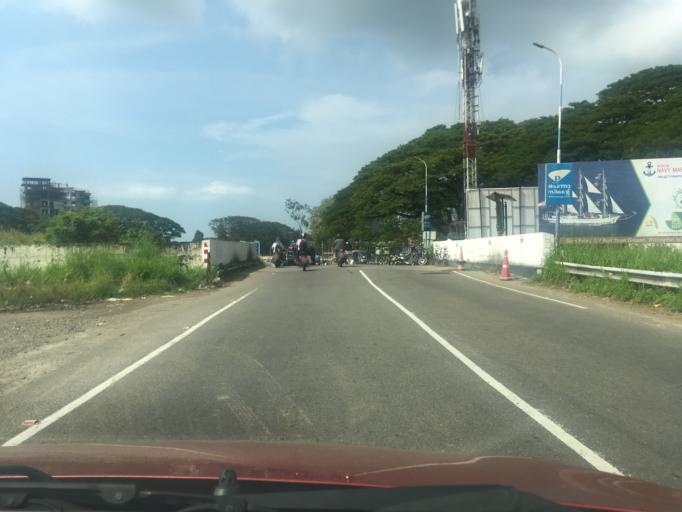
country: IN
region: Kerala
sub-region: Ernakulam
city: Cochin
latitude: 9.9450
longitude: 76.2849
